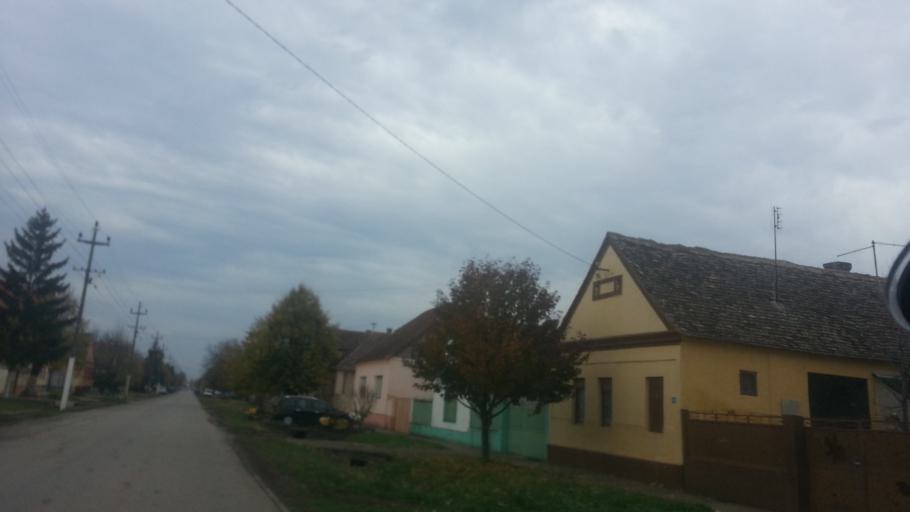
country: RS
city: Golubinci
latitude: 44.9887
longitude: 20.0622
